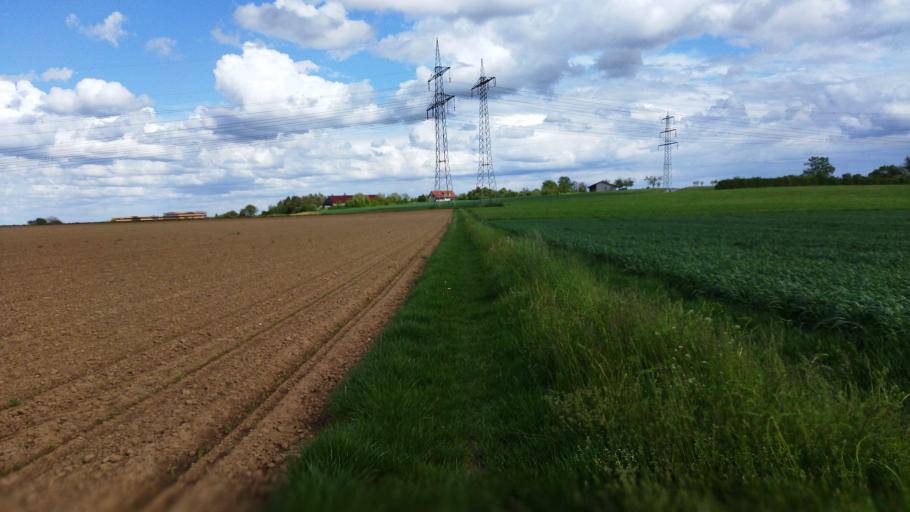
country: DE
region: Baden-Wuerttemberg
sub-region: Regierungsbezirk Stuttgart
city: Bad Wimpfen
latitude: 49.2268
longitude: 9.1304
